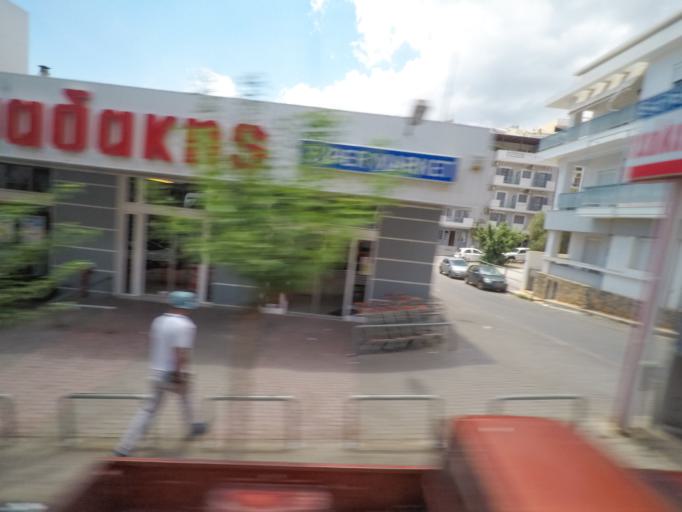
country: GR
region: Crete
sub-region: Nomos Lasithiou
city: Agios Nikolaos
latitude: 35.1927
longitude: 25.7162
